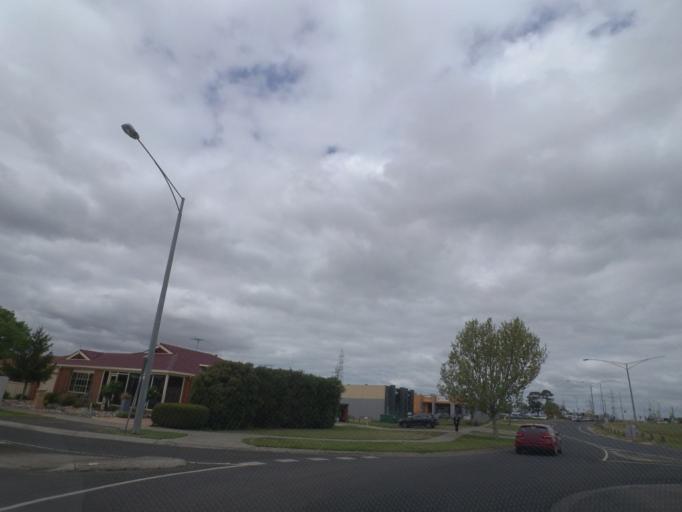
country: AU
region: Victoria
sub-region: Melton
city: Caroline Springs
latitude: -37.7601
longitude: 144.7553
